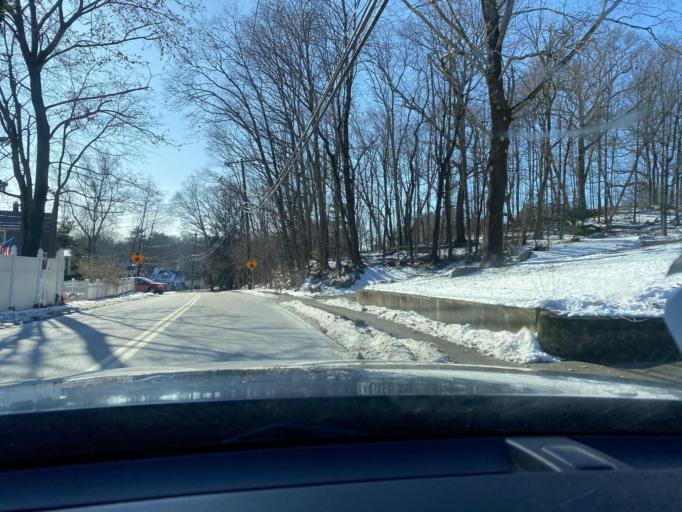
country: US
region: Massachusetts
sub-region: Norfolk County
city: Walpole
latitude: 42.1554
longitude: -71.2477
